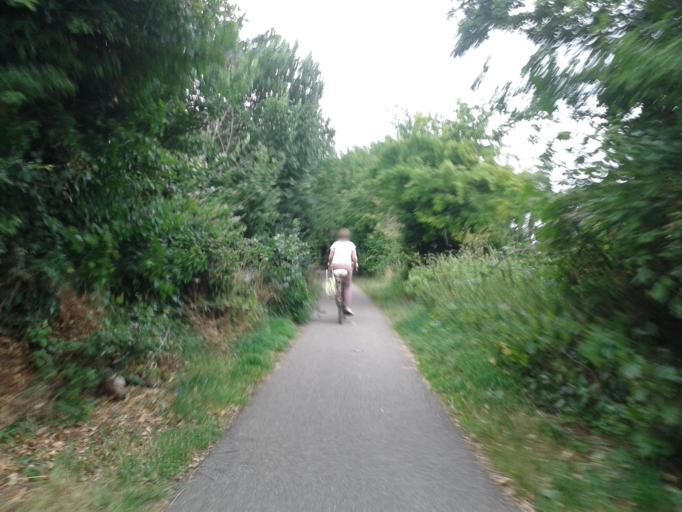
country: GB
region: England
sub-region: Cambridgeshire
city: Waterbeach
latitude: 52.2195
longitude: 0.1685
